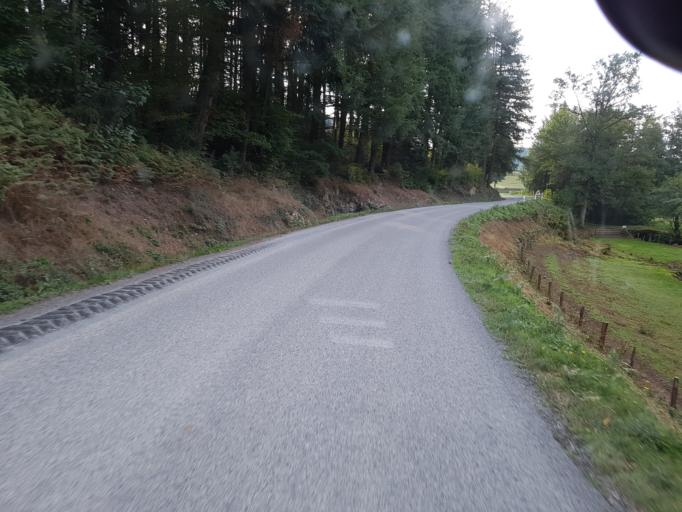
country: FR
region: Bourgogne
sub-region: Departement de Saone-et-Loire
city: Chauffailles
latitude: 46.2651
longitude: 4.3984
